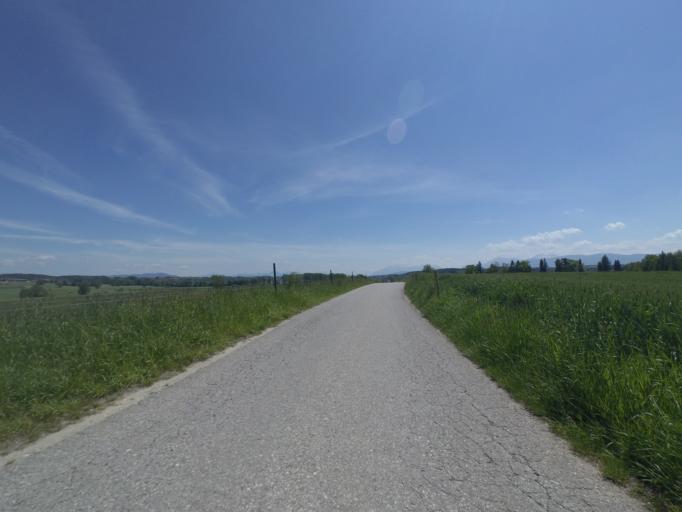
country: DE
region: Bavaria
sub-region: Upper Bavaria
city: Taching am See
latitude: 47.9514
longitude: 12.7555
